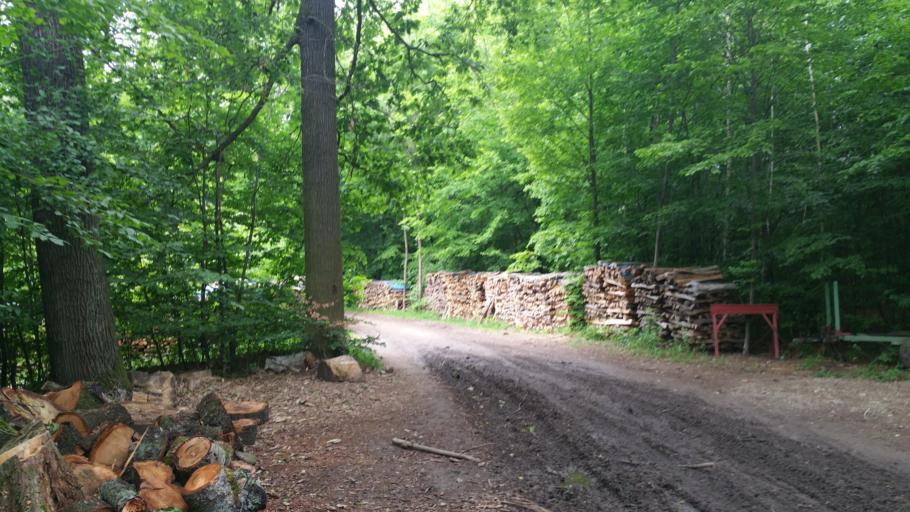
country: AT
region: Lower Austria
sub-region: Politischer Bezirk Wien-Umgebung
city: Purkersdorf
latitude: 48.2302
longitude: 16.2613
